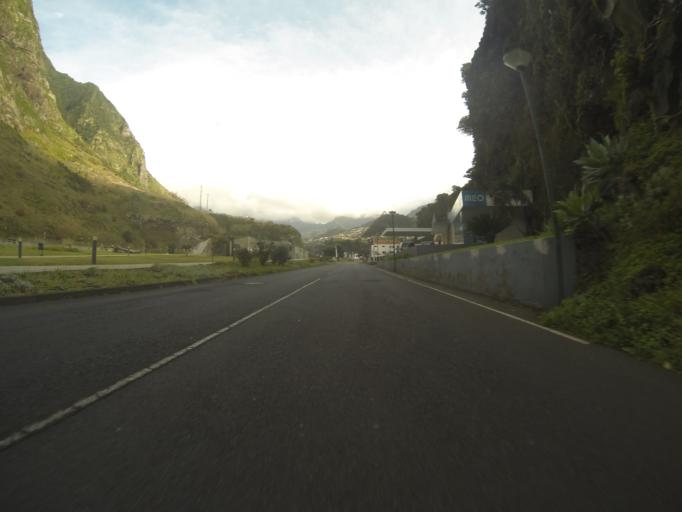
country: PT
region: Madeira
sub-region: Sao Vicente
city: Sao Vicente
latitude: 32.8060
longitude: -17.0466
